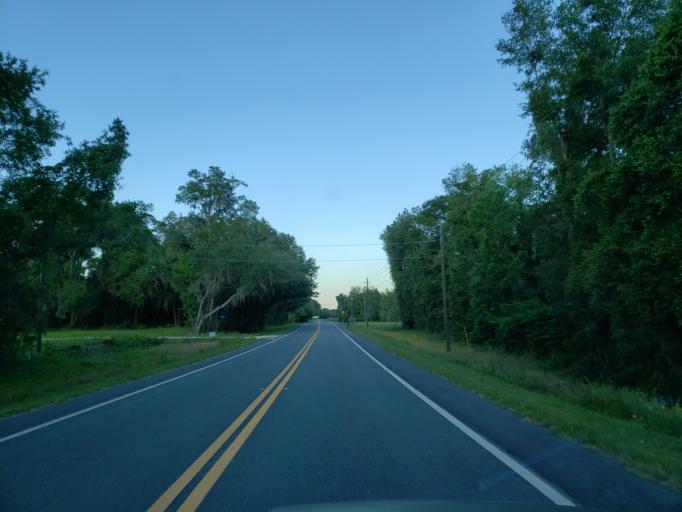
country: US
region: Georgia
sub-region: Echols County
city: Statenville
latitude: 30.5813
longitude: -83.2169
